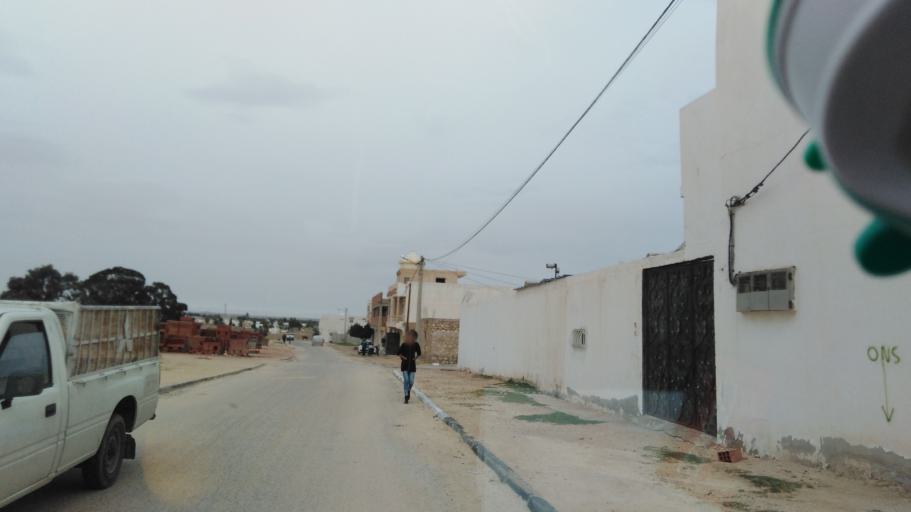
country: TN
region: Qabis
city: Gabes
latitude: 33.9534
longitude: 10.0034
